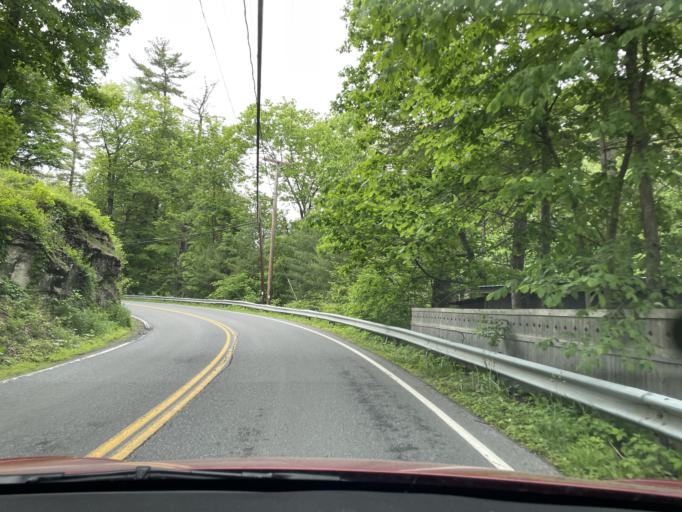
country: US
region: New York
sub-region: Ulster County
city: Zena
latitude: 42.0203
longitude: -74.0784
